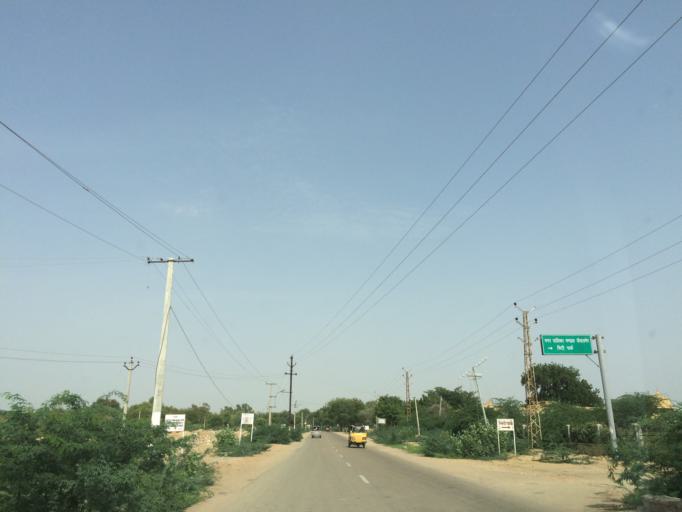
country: IN
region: Rajasthan
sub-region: Jaisalmer
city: Jaisalmer
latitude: 26.9113
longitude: 70.9279
